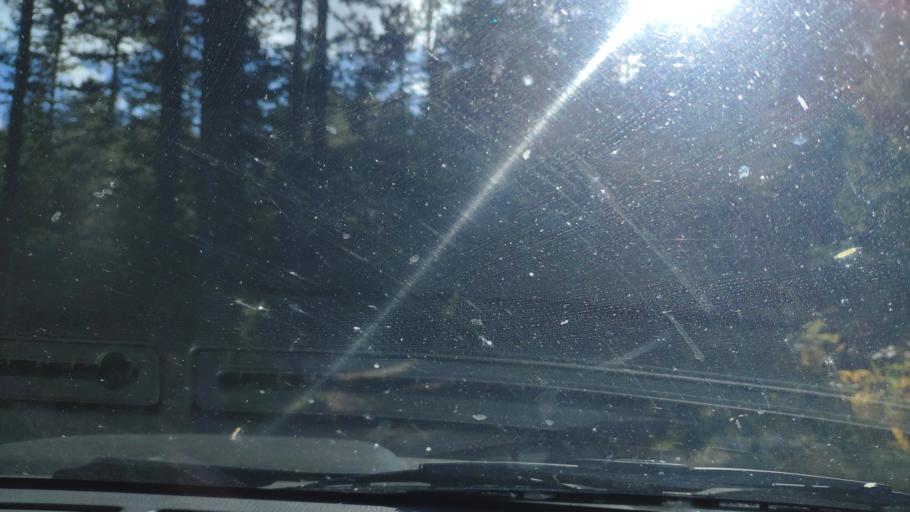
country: AL
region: Korce
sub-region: Rrethi i Devollit
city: Miras
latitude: 40.3920
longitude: 20.8866
